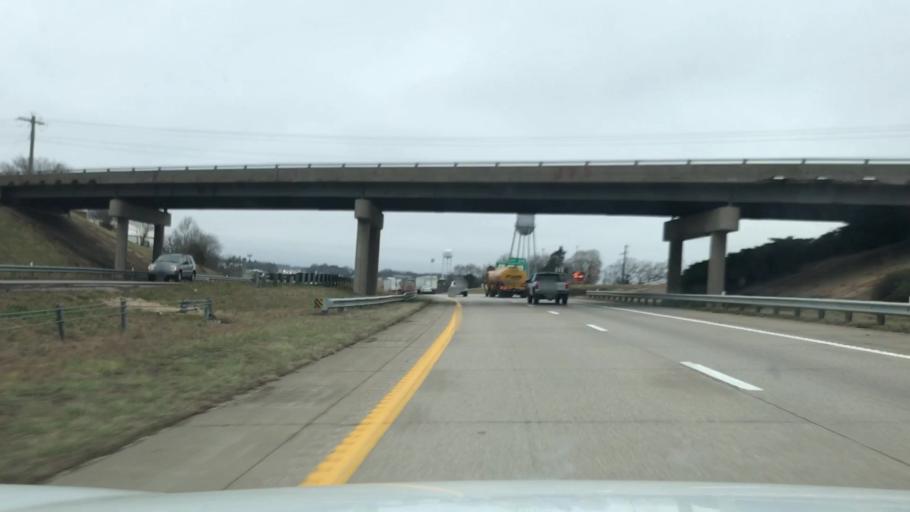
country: US
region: Missouri
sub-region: Crawford County
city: Bourbon
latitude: 38.1590
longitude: -91.2435
